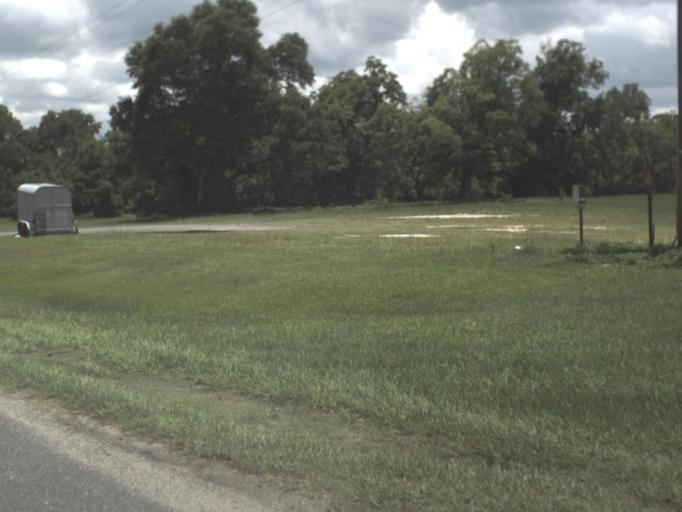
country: US
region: Florida
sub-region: Union County
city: Lake Butler
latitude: 30.0176
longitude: -82.3512
